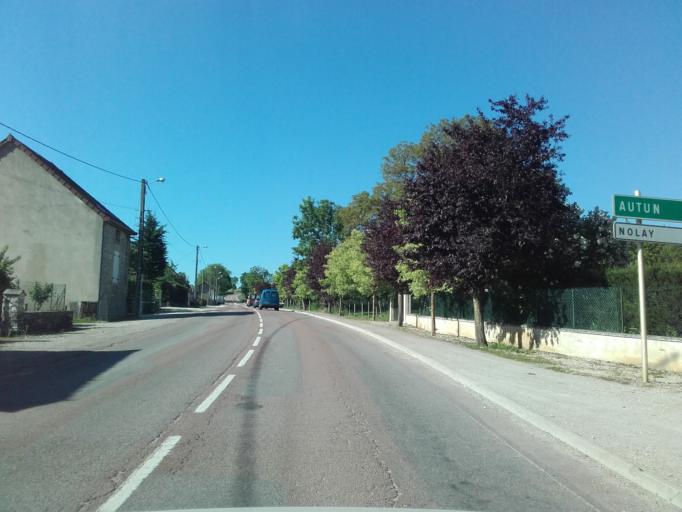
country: FR
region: Bourgogne
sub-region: Departement de la Cote-d'Or
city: Nolay
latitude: 46.9541
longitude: 4.6742
